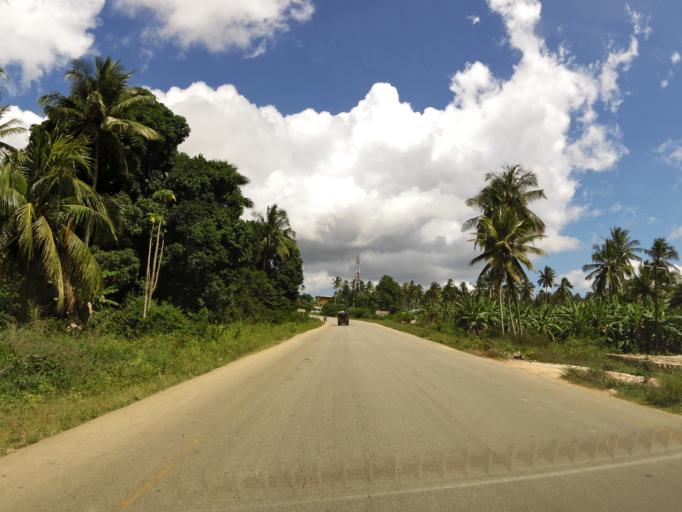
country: TZ
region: Zanzibar Central/South
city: Koani
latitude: -6.1358
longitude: 39.2907
